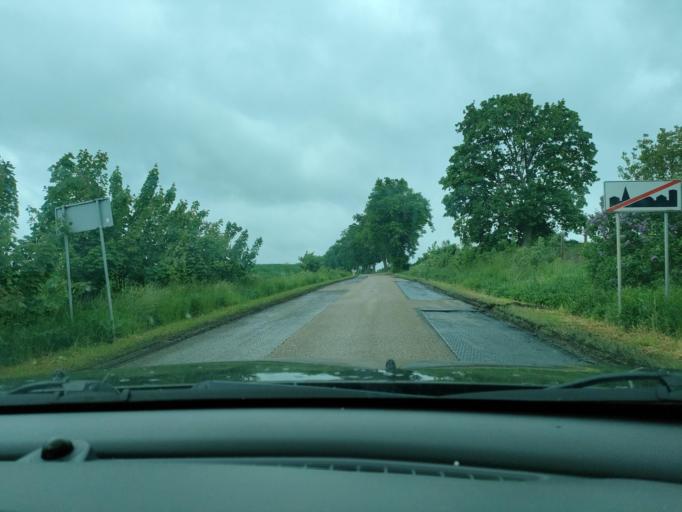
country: PL
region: Pomeranian Voivodeship
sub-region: Powiat kwidzynski
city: Gardeja
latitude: 53.5678
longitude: 19.0086
